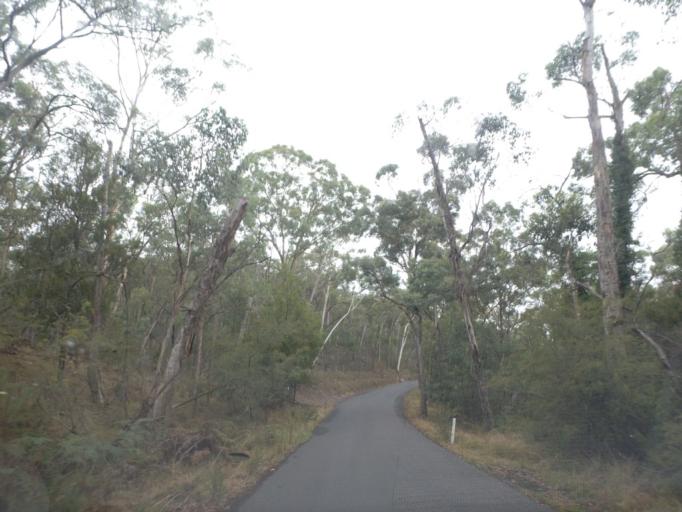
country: AU
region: Victoria
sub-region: Nillumbik
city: Saint Andrews
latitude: -37.6464
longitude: 145.2851
